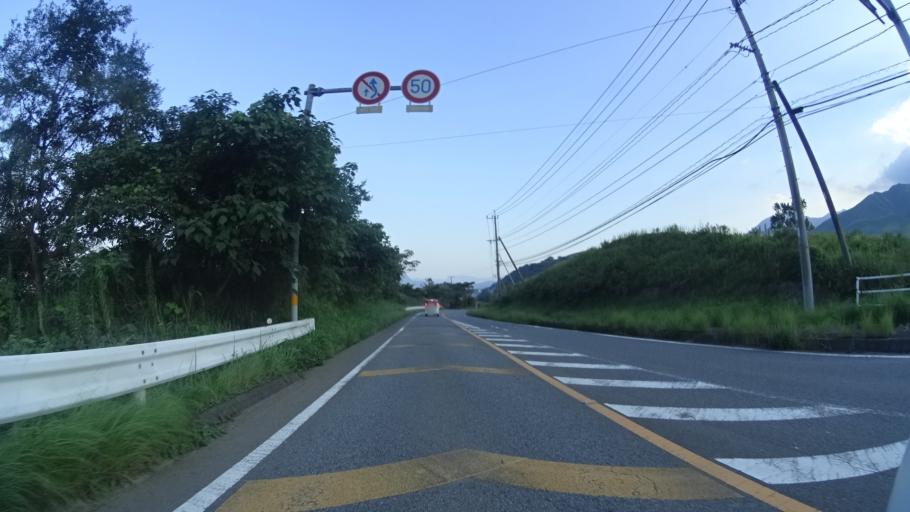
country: JP
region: Oita
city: Beppu
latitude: 33.3454
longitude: 131.4567
